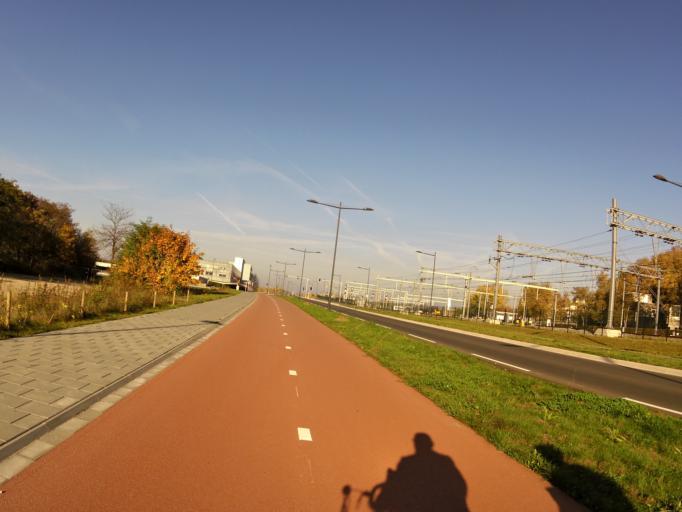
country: NL
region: North Brabant
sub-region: Gemeente 's-Hertogenbosch
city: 's-Hertogenbosch
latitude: 51.6949
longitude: 5.2947
